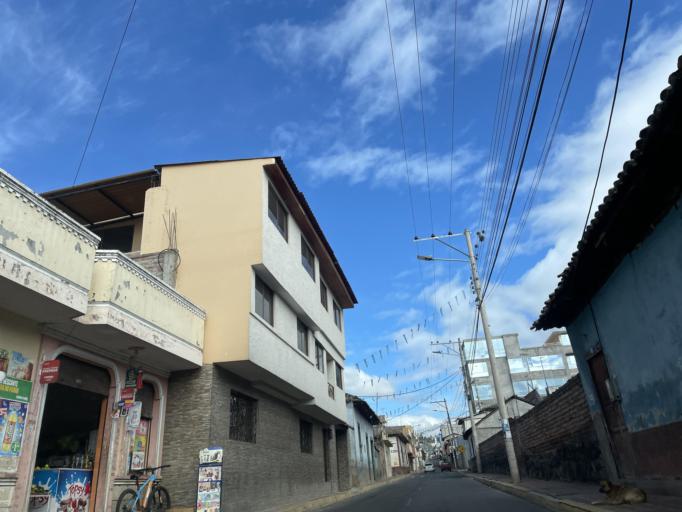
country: EC
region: Chimborazo
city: Guano
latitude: -1.6077
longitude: -78.6375
